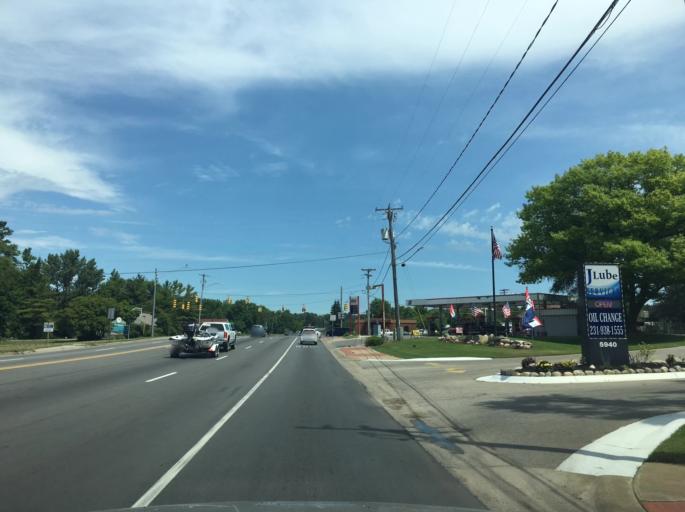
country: US
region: Michigan
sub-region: Grand Traverse County
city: Traverse City
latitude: 44.7726
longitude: -85.5012
